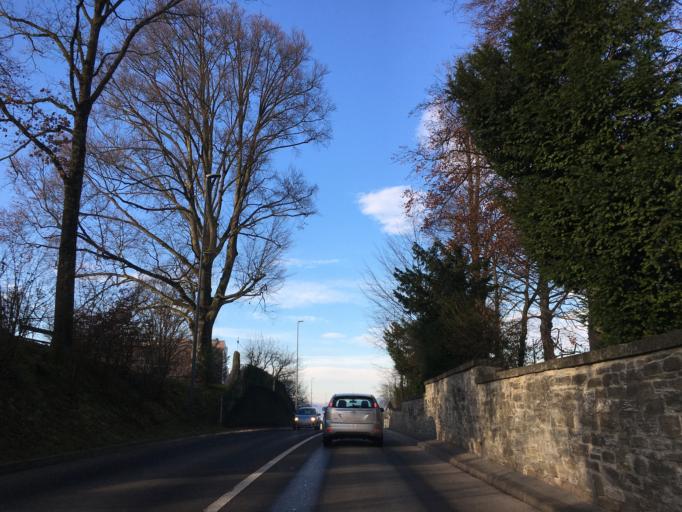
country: CH
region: Lucerne
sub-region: Lucerne-Land District
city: Adligenswil
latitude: 47.0511
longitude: 8.3551
